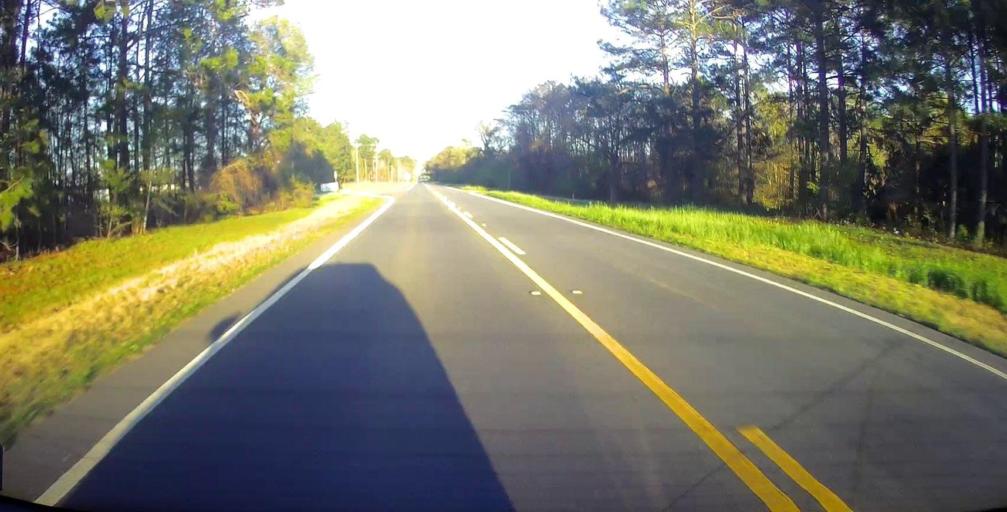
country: US
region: Georgia
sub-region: Wilcox County
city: Rochelle
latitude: 31.9497
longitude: -83.4858
